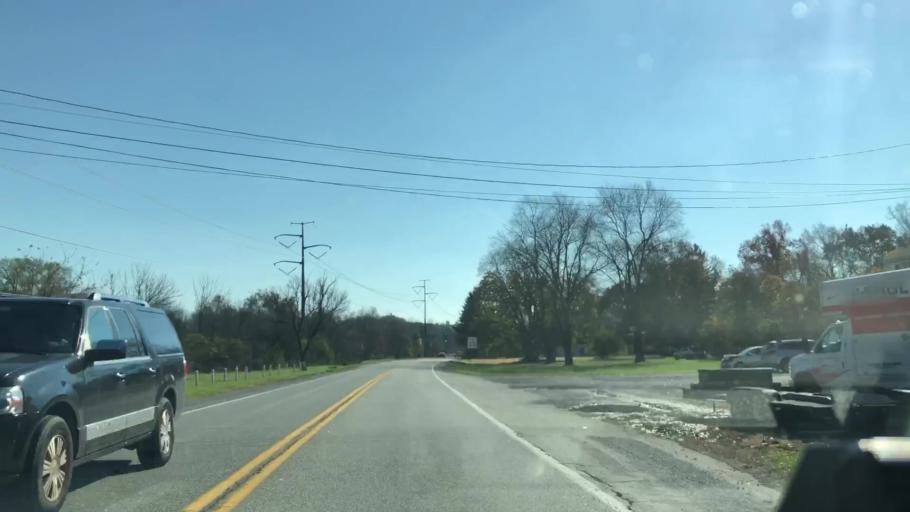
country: US
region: Pennsylvania
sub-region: Montgomery County
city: Sanatoga
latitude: 40.2021
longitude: -75.5859
